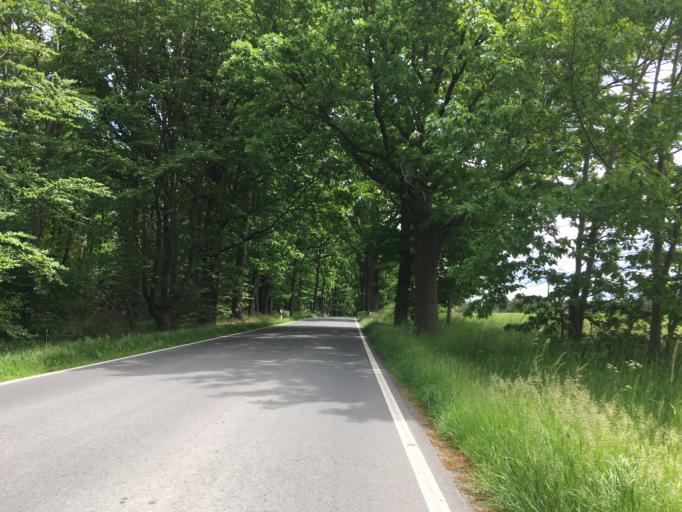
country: DE
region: Brandenburg
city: Falkenberg
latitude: 52.7670
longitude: 13.9623
